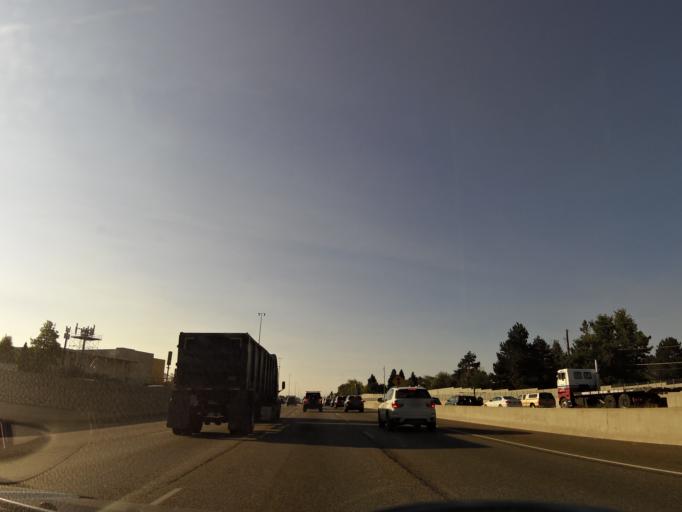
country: US
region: Colorado
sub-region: Arapahoe County
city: Cherry Hills Village
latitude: 39.6519
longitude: -104.9179
